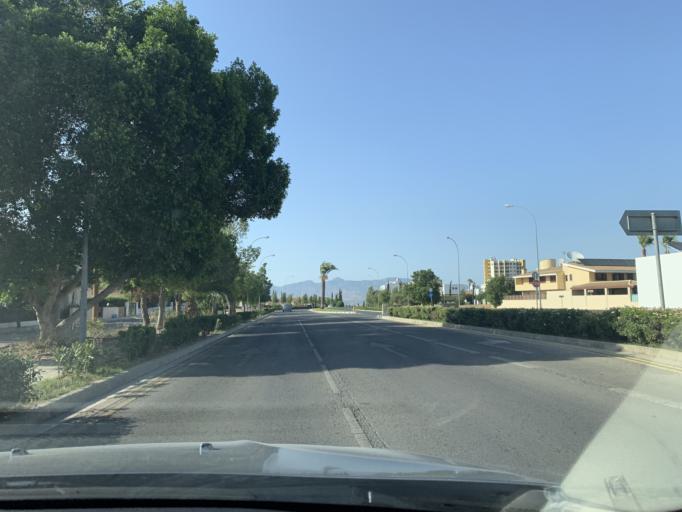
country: CY
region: Lefkosia
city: Nicosia
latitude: 35.1494
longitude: 33.3813
